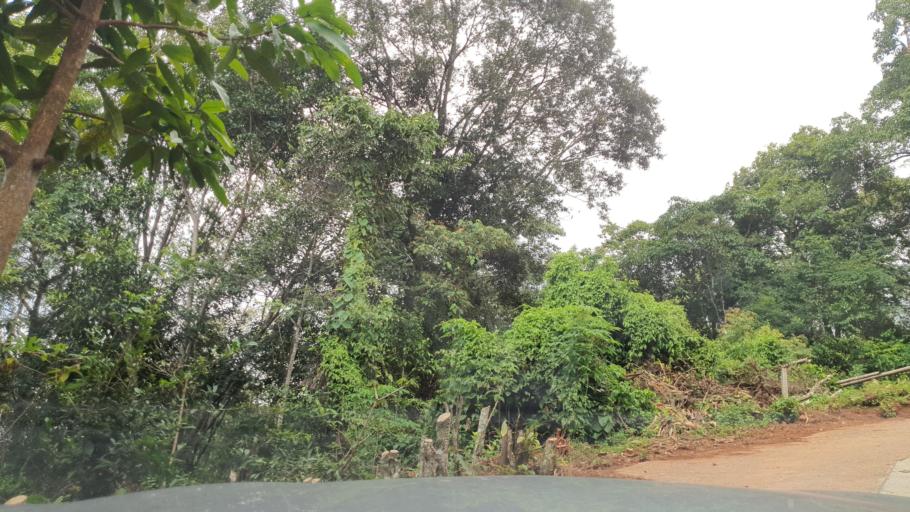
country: TH
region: Chiang Mai
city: Mae On
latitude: 18.9540
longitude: 99.2970
